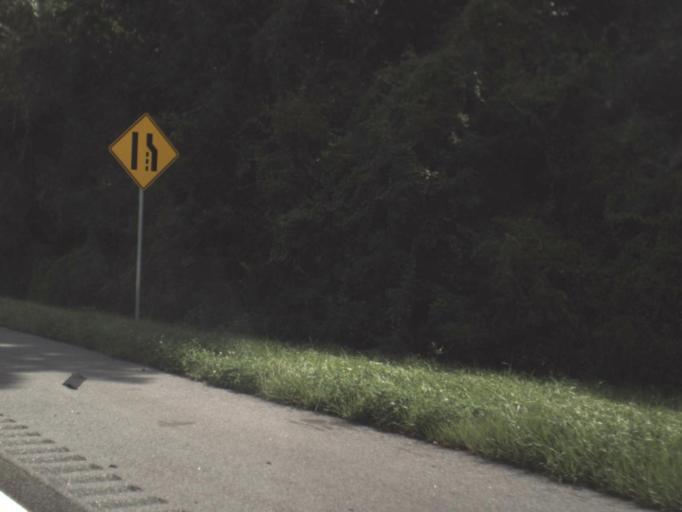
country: US
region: Florida
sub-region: Hillsborough County
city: Lutz
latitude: 28.1539
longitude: -82.4057
